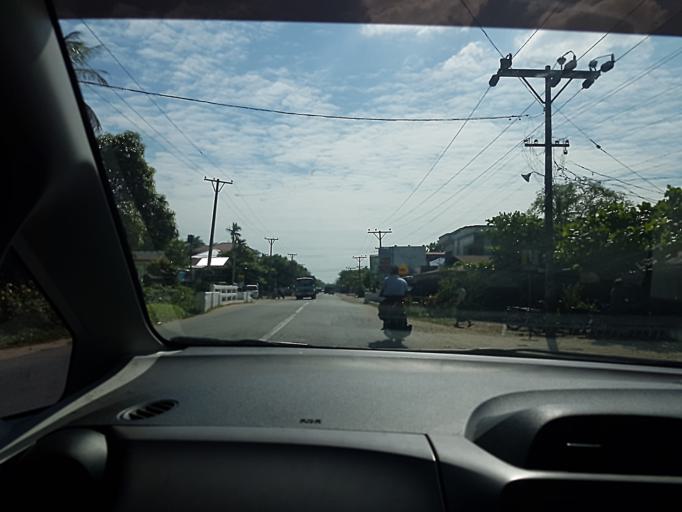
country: MM
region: Mon
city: Thaton
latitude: 16.6976
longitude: 97.4249
